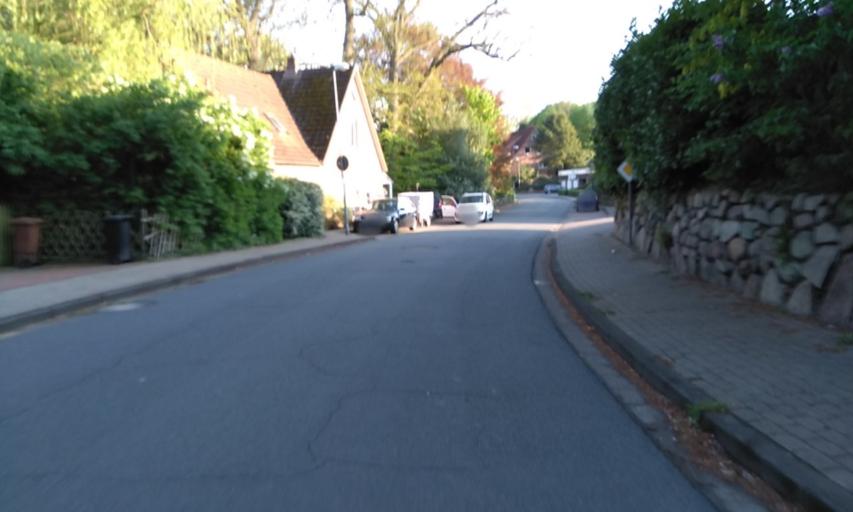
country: DE
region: Lower Saxony
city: Dollern
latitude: 53.5385
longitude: 9.5483
